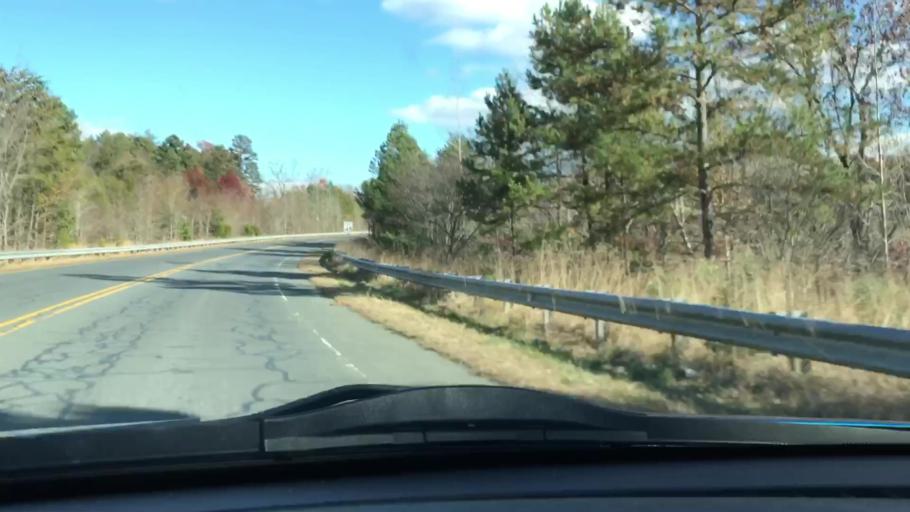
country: US
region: North Carolina
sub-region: Randolph County
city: Asheboro
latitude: 35.7196
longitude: -79.7763
